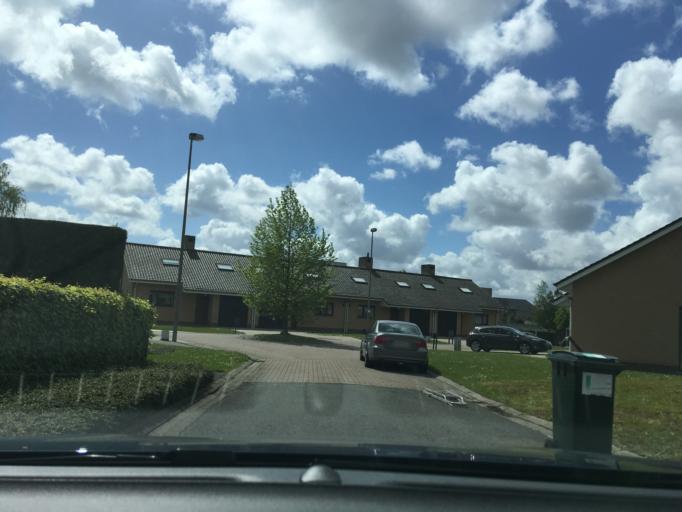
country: BE
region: Flanders
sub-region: Provincie West-Vlaanderen
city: Hooglede
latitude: 50.9954
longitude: 3.1009
